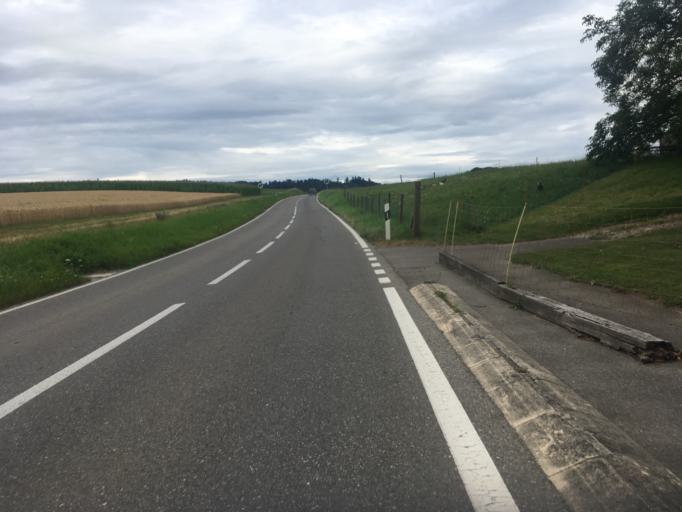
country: CH
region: Bern
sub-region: Seeland District
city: Erlach
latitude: 47.0330
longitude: 7.0937
